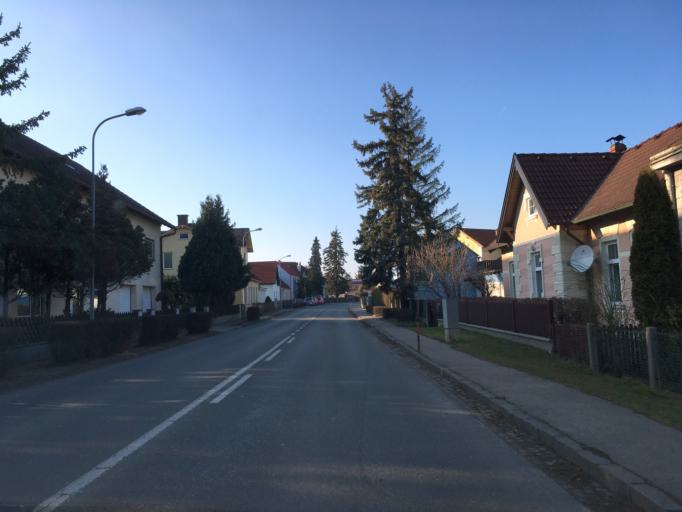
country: AT
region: Lower Austria
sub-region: Politischer Bezirk Tulln
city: Wordern
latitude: 48.3265
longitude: 16.1813
